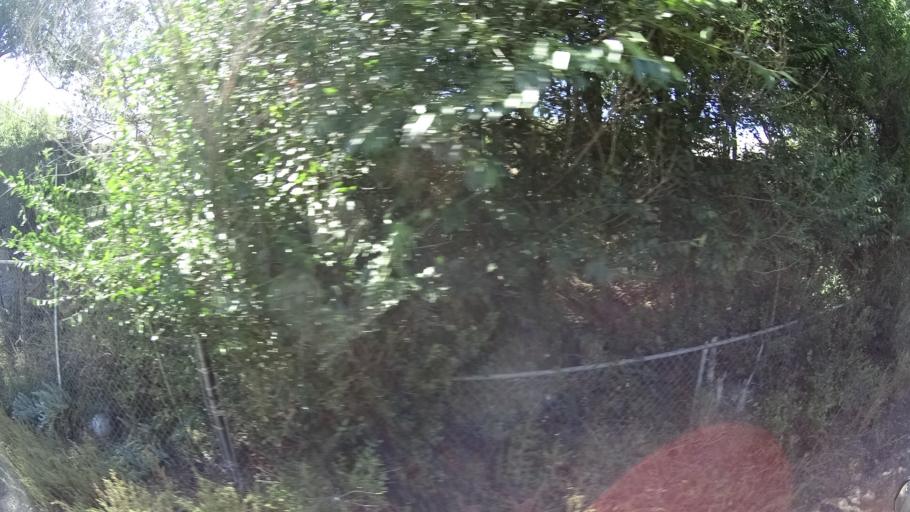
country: US
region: Colorado
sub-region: El Paso County
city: Colorado Springs
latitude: 38.8635
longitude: -104.8603
